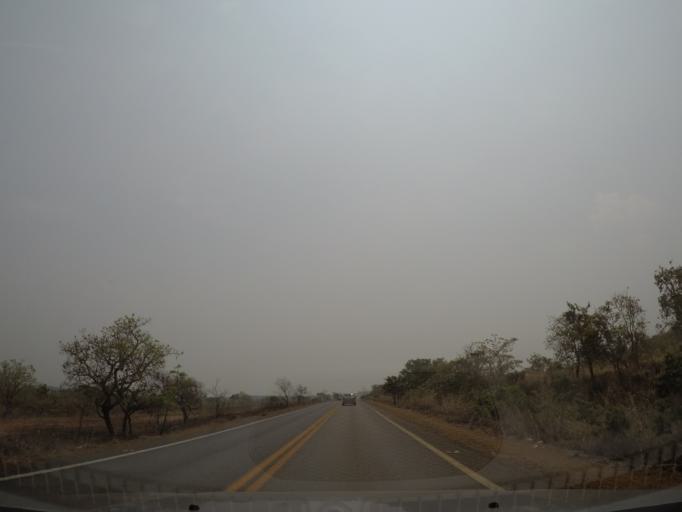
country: BR
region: Goias
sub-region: Pirenopolis
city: Pirenopolis
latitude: -15.8930
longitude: -48.8866
